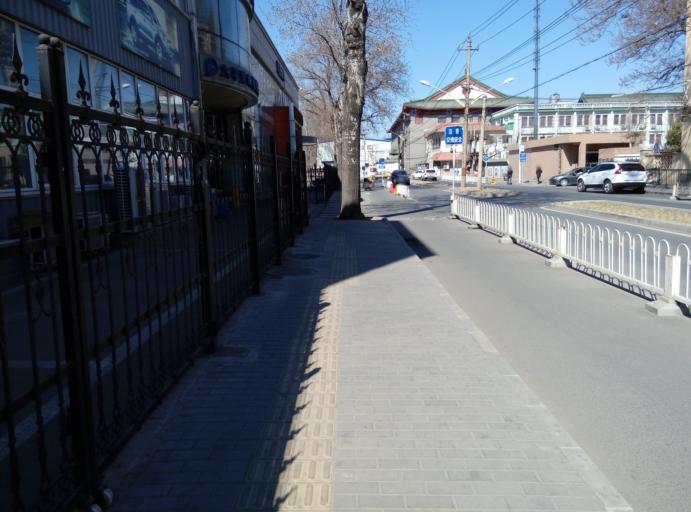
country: CN
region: Beijing
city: Haidian
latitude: 39.9916
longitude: 116.2864
